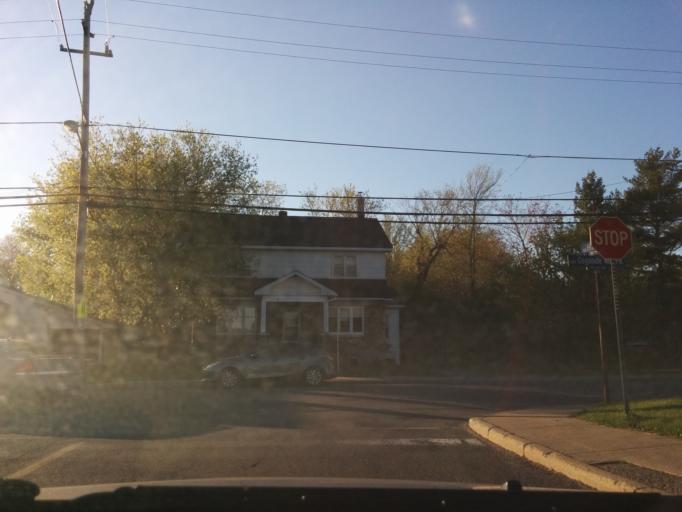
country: CA
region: Ontario
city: Ottawa
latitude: 45.1458
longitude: -75.6063
